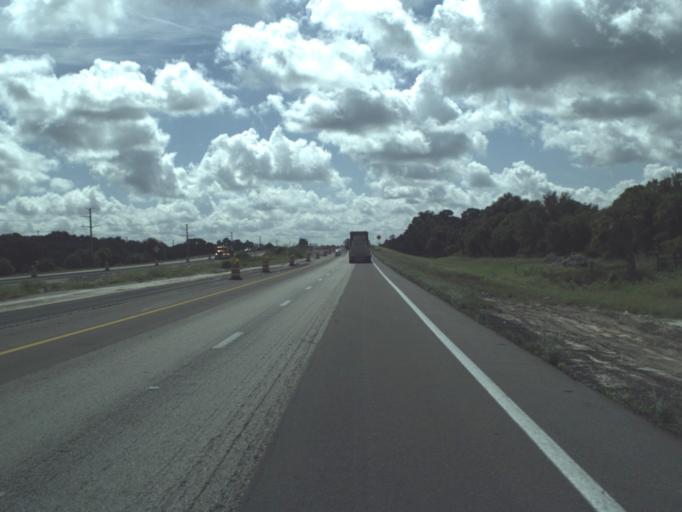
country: US
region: Florida
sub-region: Charlotte County
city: Port Charlotte
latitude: 27.0633
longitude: -82.0890
